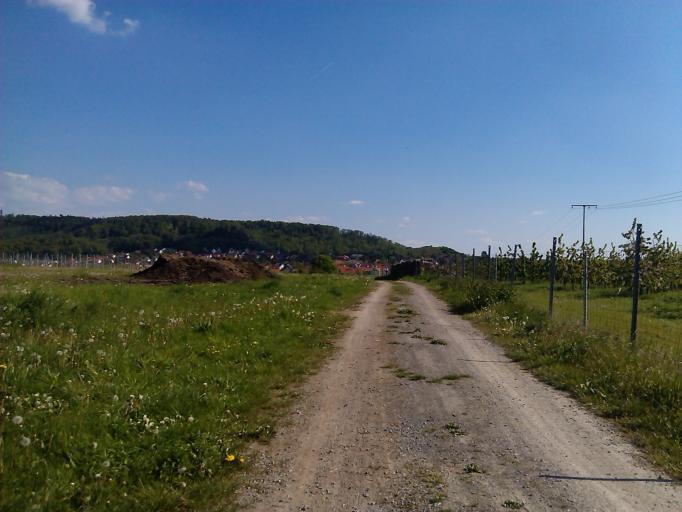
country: DE
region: Baden-Wuerttemberg
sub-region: Karlsruhe Region
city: Sternenfels
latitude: 49.0609
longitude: 8.8446
